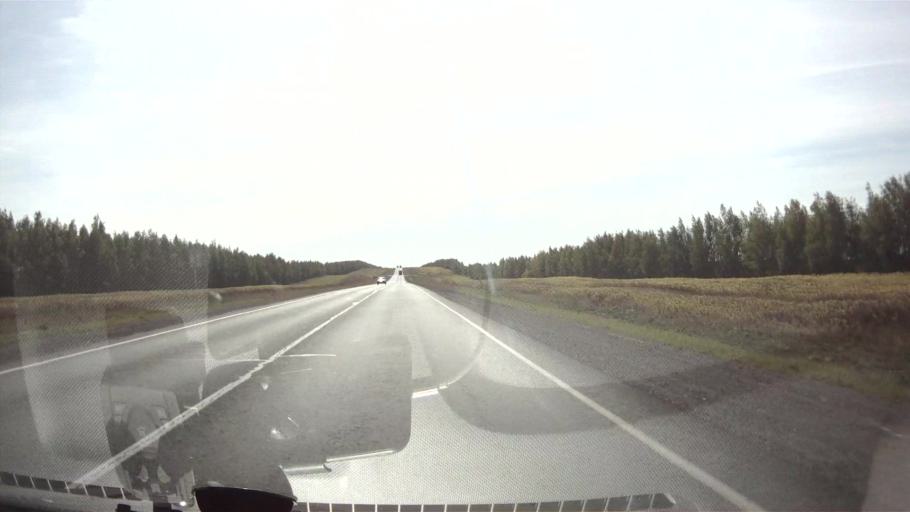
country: RU
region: Samara
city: Syzran'
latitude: 52.9194
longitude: 48.3021
